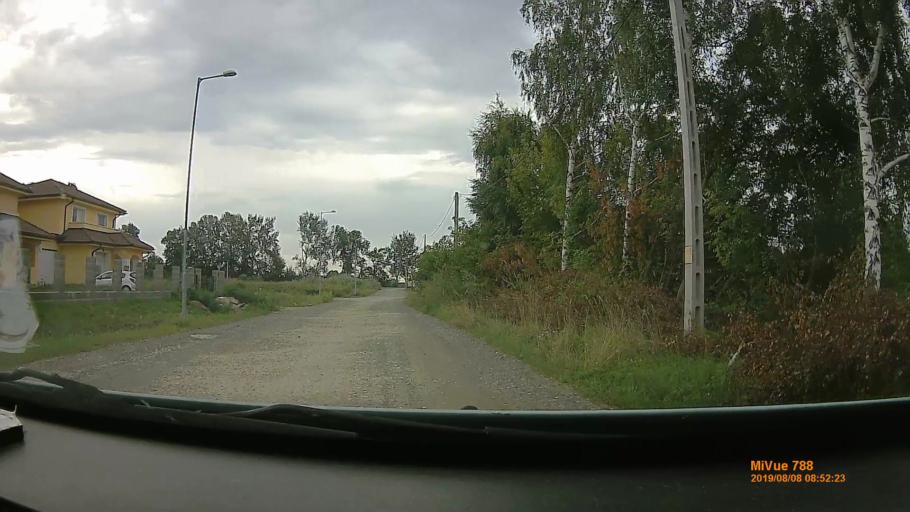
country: HU
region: Hajdu-Bihar
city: Debrecen
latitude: 47.5994
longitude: 21.6464
